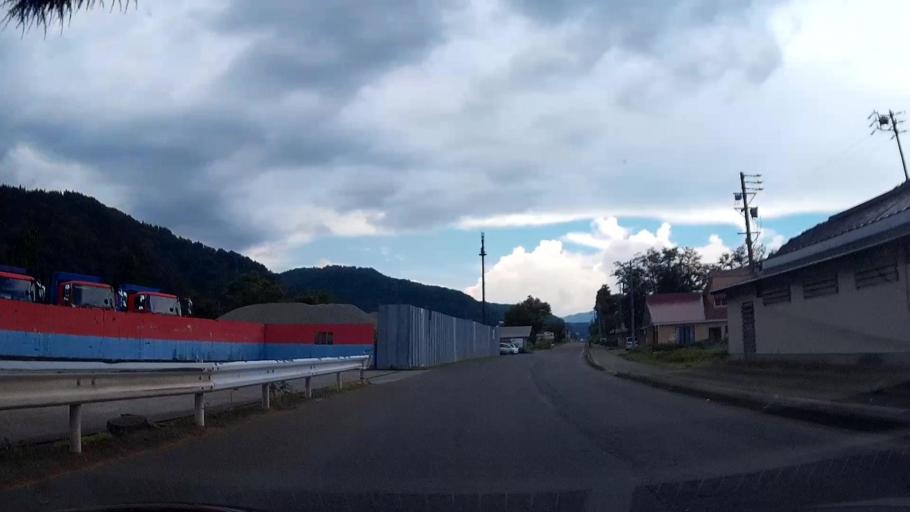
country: JP
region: Nagano
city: Iiyama
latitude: 36.9820
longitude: 138.5039
